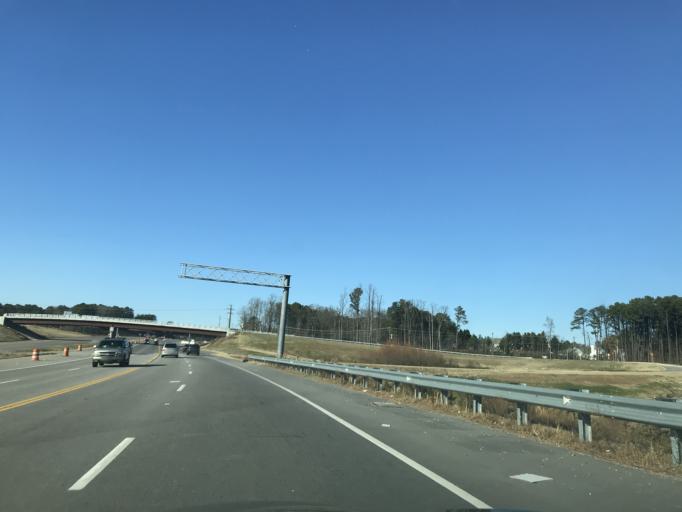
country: US
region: North Carolina
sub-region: Durham County
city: Durham
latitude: 35.9795
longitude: -78.8554
